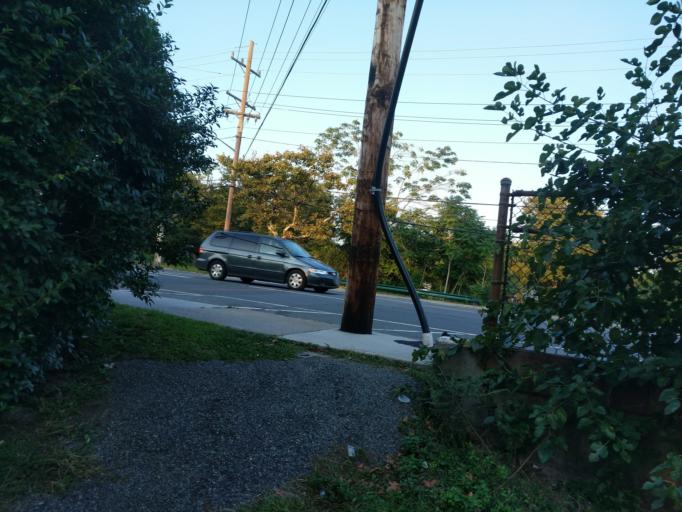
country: US
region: New York
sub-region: Nassau County
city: Valley Stream
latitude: 40.6586
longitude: -73.7099
